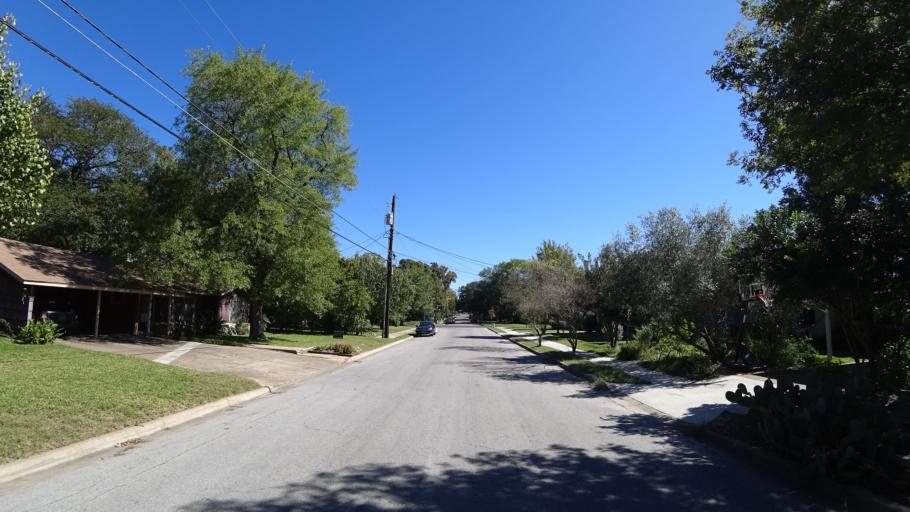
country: US
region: Texas
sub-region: Travis County
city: Austin
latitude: 30.3345
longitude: -97.7267
